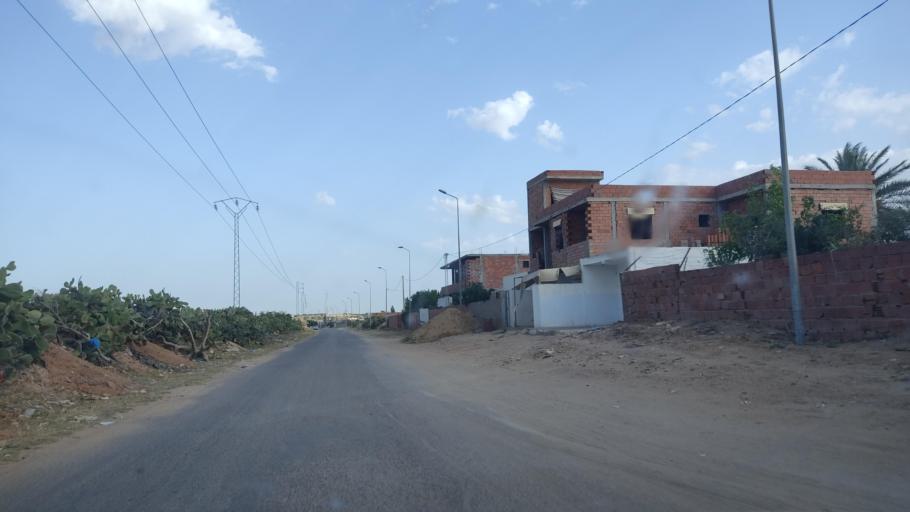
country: TN
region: Safaqis
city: Sfax
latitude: 34.8495
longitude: 10.6127
